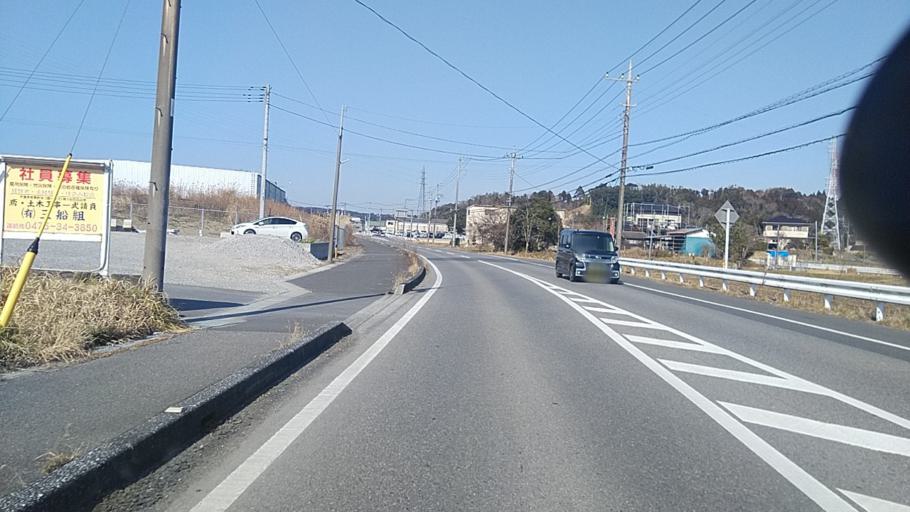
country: JP
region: Chiba
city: Mobara
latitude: 35.4687
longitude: 140.2825
